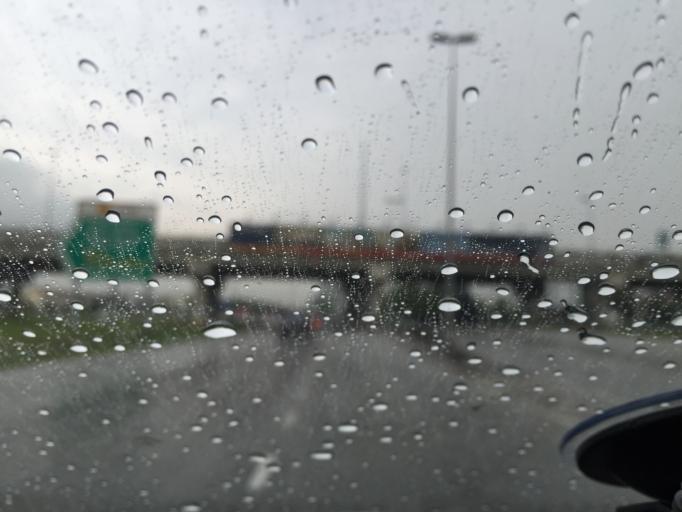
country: MY
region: Selangor
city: Subang Jaya
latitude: 3.0182
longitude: 101.5324
